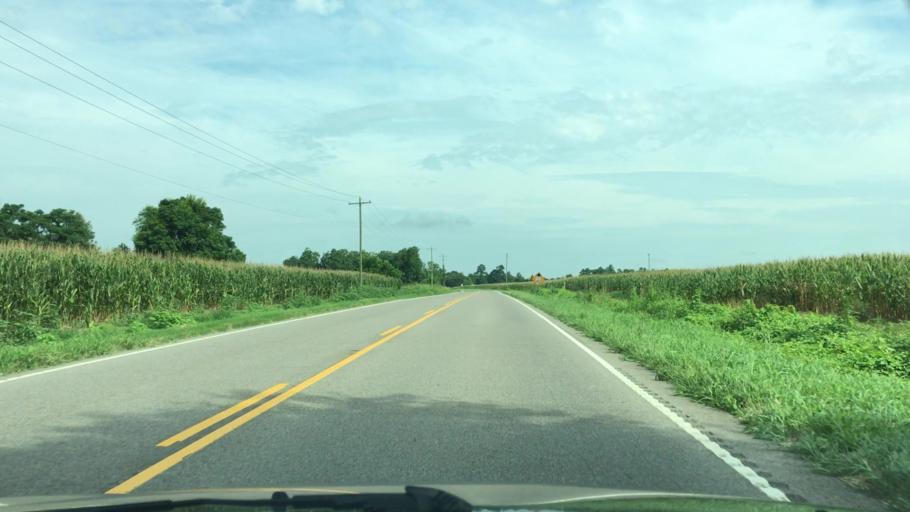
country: US
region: South Carolina
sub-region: Lexington County
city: Batesburg-Leesville
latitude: 33.6957
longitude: -81.4758
